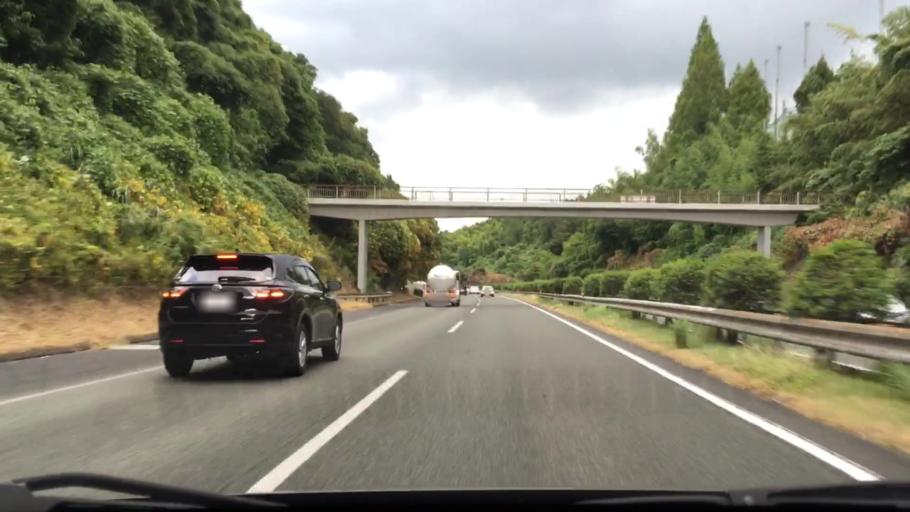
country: JP
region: Fukuoka
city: Miyata
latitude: 33.7475
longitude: 130.5944
